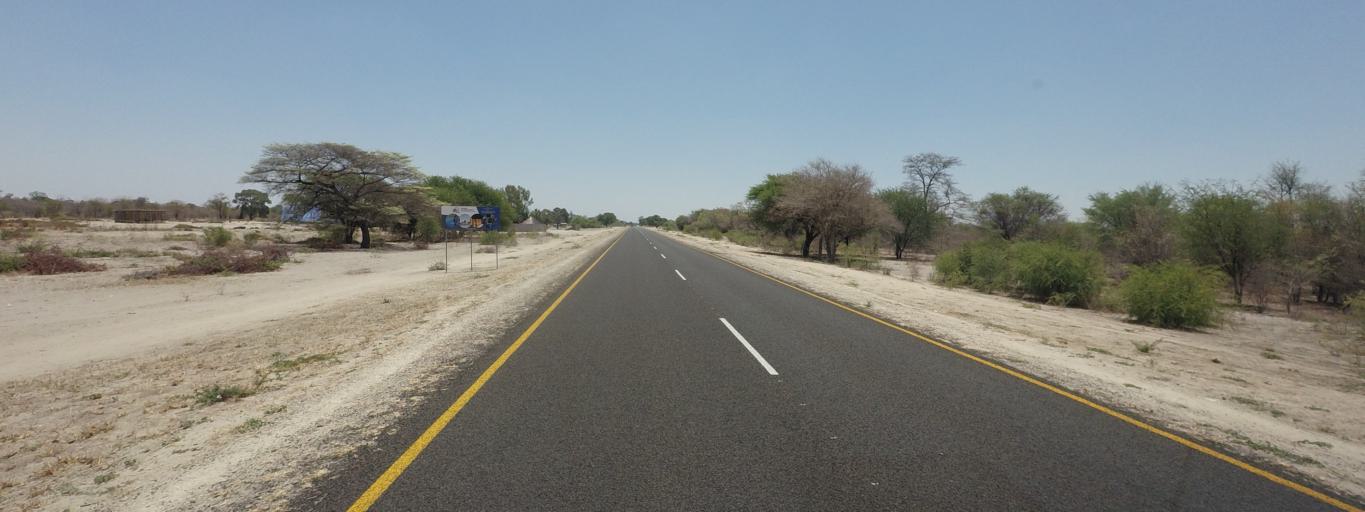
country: ZM
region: Western
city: Sesheke
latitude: -17.7333
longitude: 24.5362
